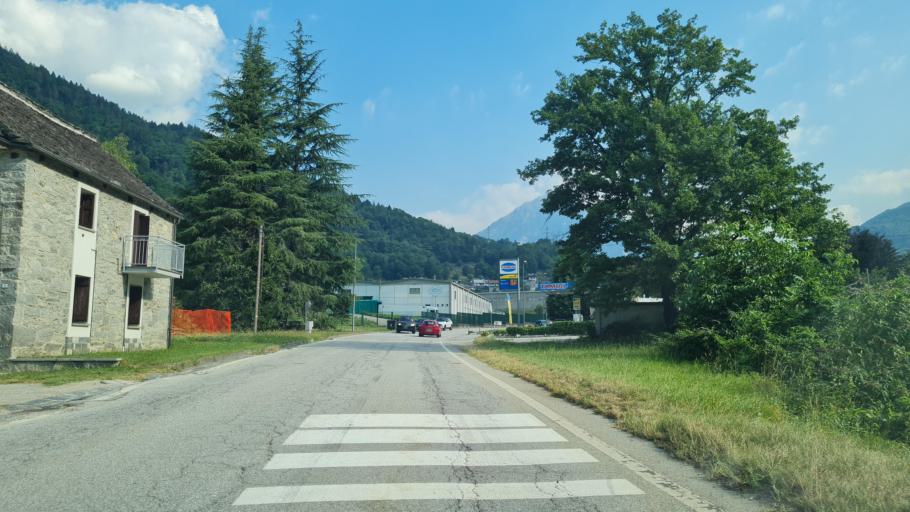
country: IT
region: Piedmont
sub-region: Provincia Verbano-Cusio-Ossola
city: Crodo
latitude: 46.2059
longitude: 8.3191
